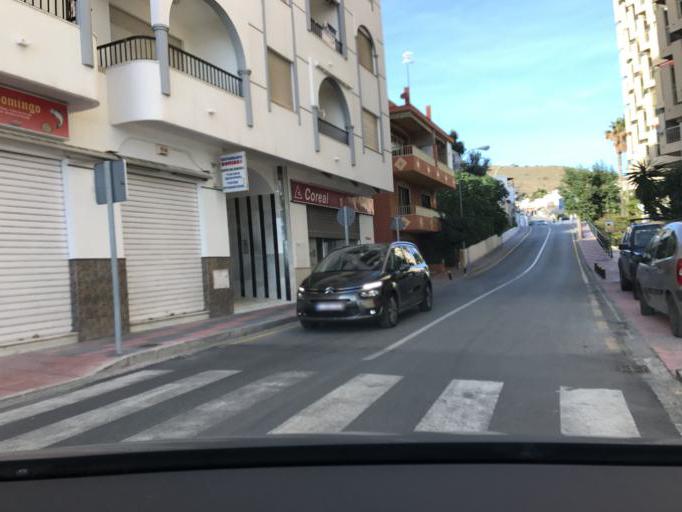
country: ES
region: Andalusia
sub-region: Provincia de Granada
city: Almunecar
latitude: 36.7342
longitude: -3.7029
